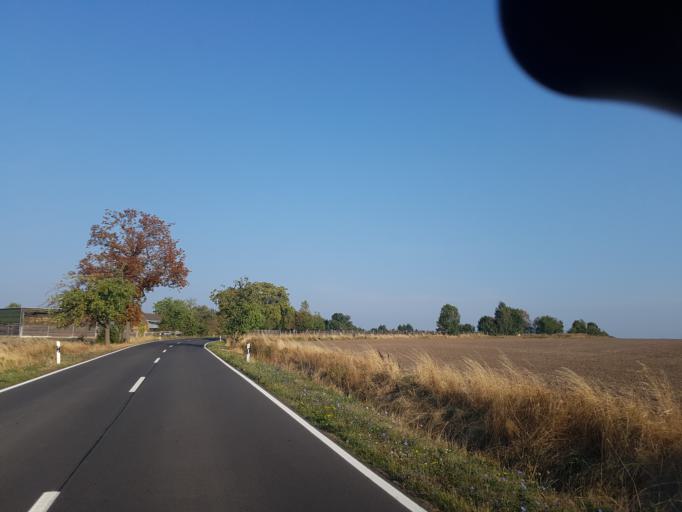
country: DE
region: Saxony-Anhalt
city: Nudersdorf
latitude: 51.9655
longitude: 12.5740
